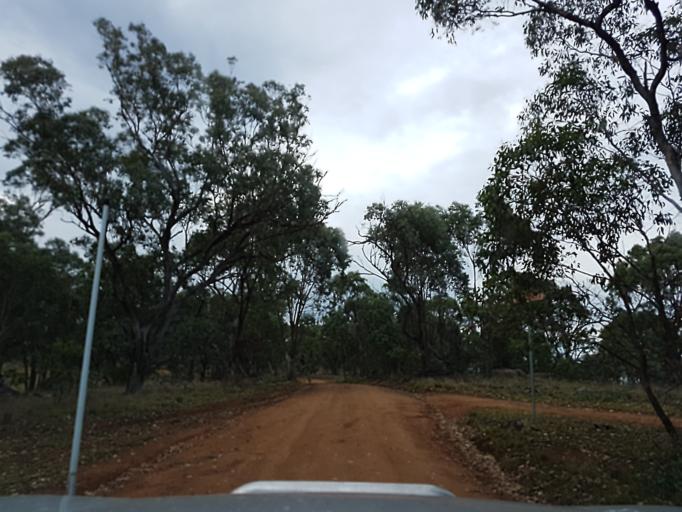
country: AU
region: New South Wales
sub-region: Snowy River
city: Jindabyne
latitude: -36.9604
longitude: 148.3779
